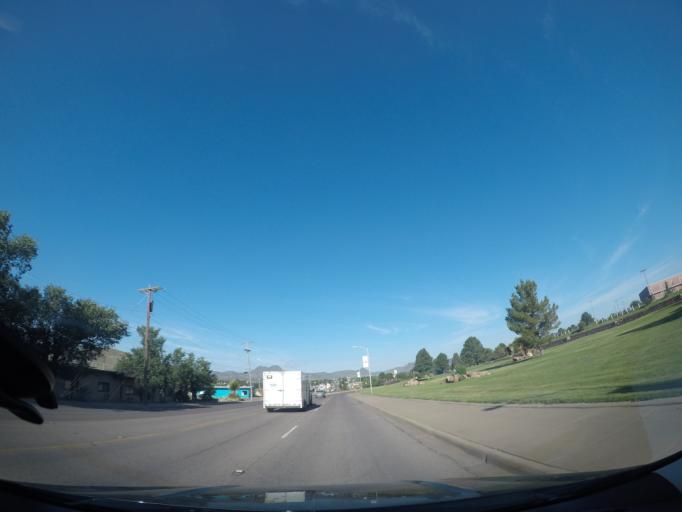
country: US
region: Texas
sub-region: Brewster County
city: Alpine
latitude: 30.3611
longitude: -103.6501
